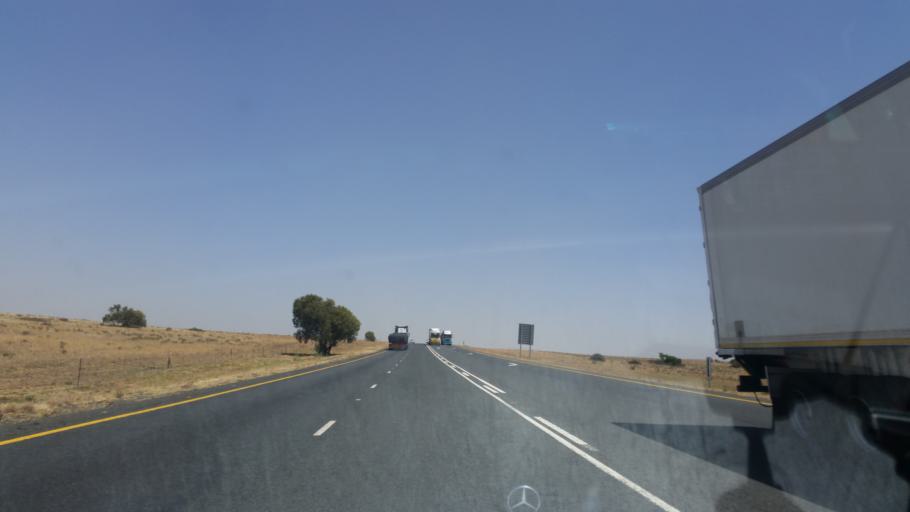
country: ZA
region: Orange Free State
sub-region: Lejweleputswa District Municipality
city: Winburg
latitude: -28.7044
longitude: 26.7934
